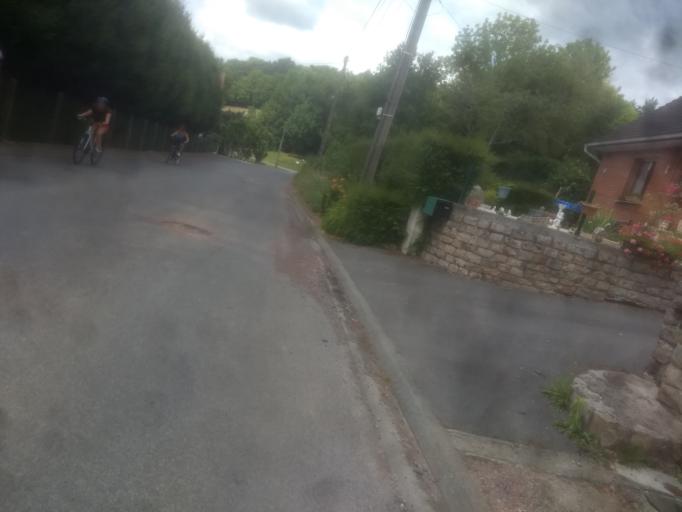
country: FR
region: Nord-Pas-de-Calais
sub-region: Departement du Pas-de-Calais
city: Mont-Saint-Eloi
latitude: 50.3391
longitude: 2.6914
